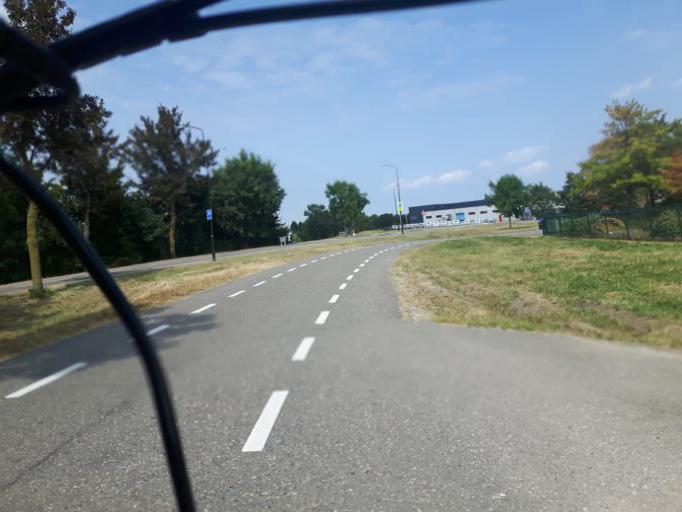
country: NL
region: Gelderland
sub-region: Gemeente Zaltbommel
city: Zaltbommel
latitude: 51.8178
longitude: 5.2164
